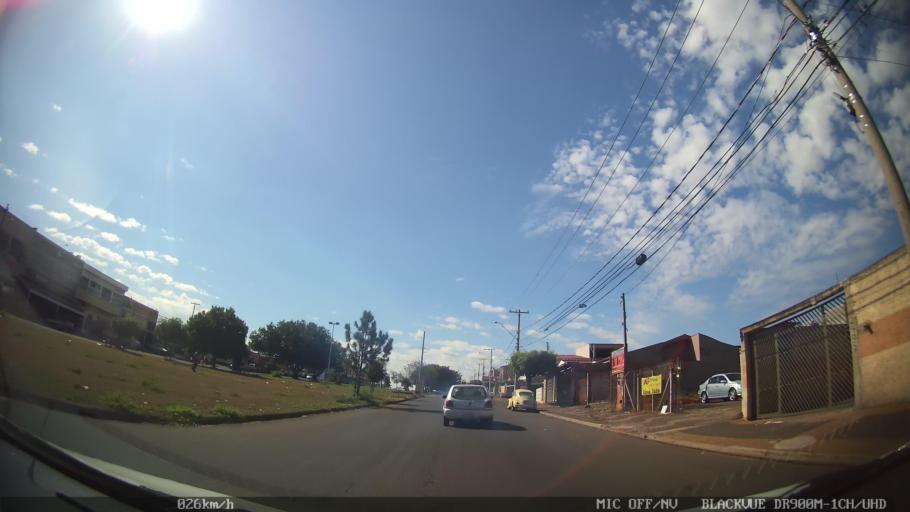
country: BR
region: Sao Paulo
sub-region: Santa Barbara D'Oeste
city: Santa Barbara d'Oeste
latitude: -22.7341
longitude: -47.3867
